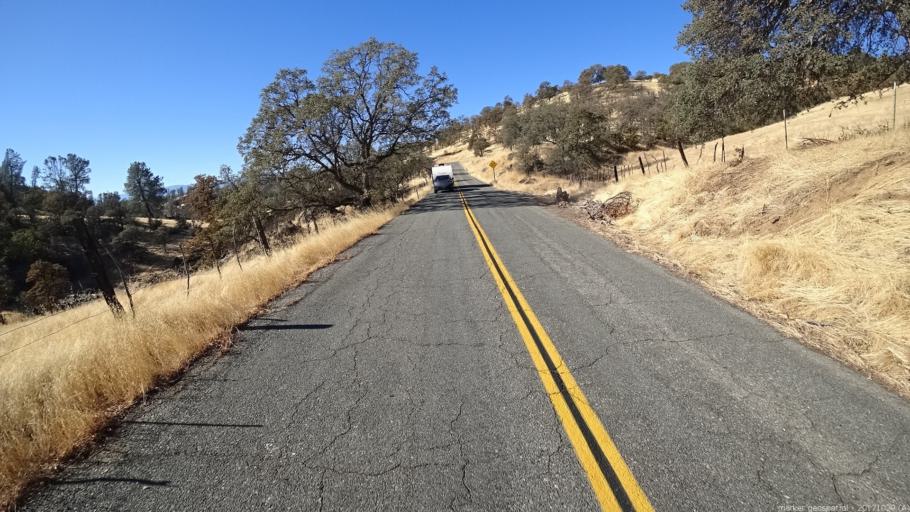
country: US
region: California
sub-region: Trinity County
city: Lewiston
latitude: 40.4066
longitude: -122.7708
